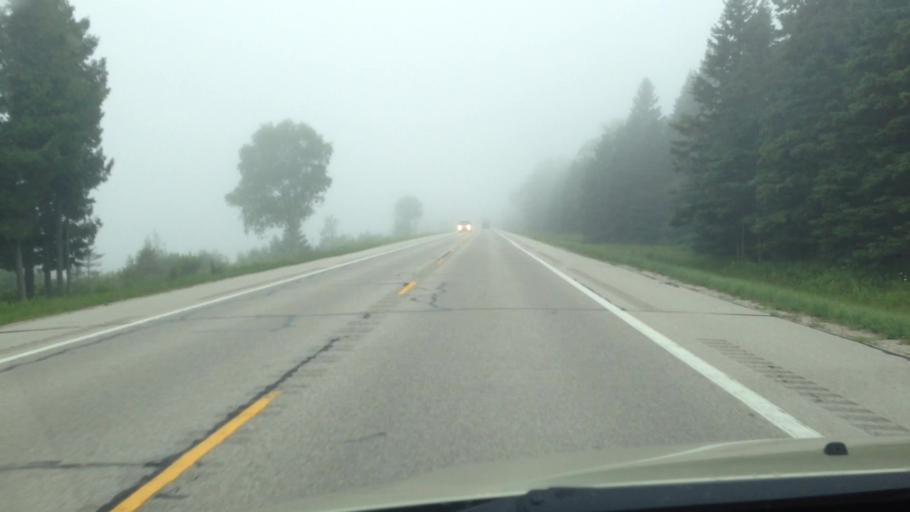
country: US
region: Michigan
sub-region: Luce County
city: Newberry
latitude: 46.1008
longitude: -85.4088
